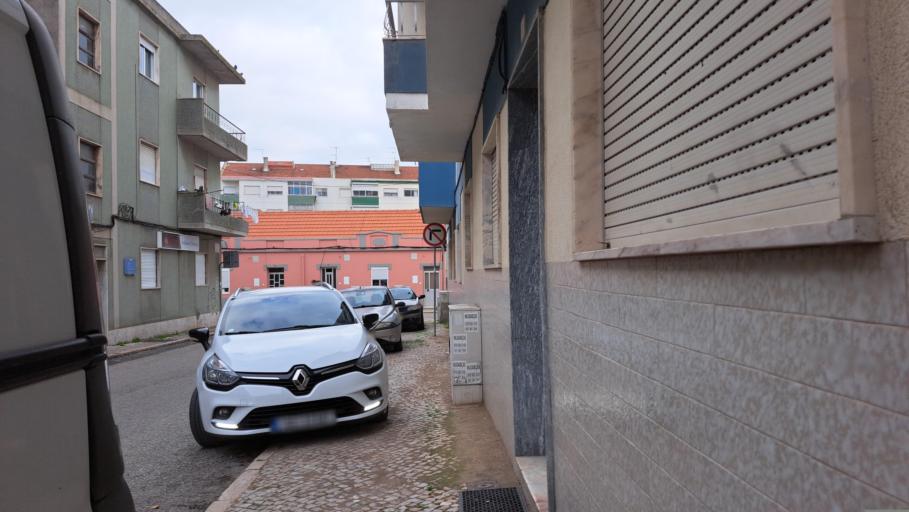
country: PT
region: Setubal
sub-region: Moita
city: Alhos Vedros
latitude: 38.6576
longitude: -9.0409
